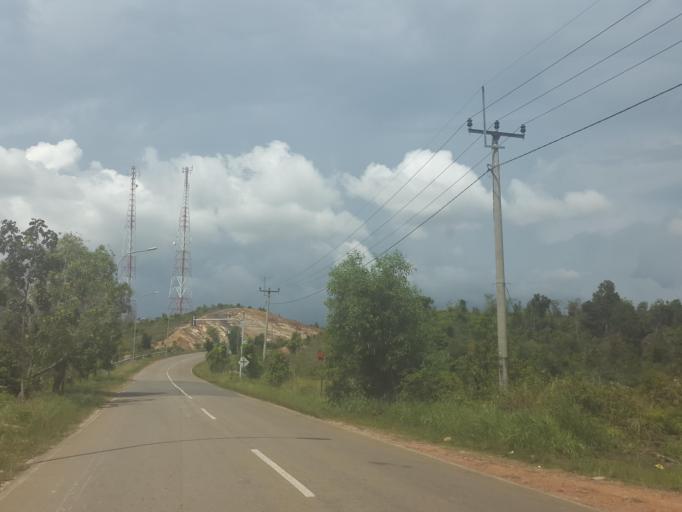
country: ID
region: Riau Islands
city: Tanjungpinang
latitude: 0.9514
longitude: 104.0724
